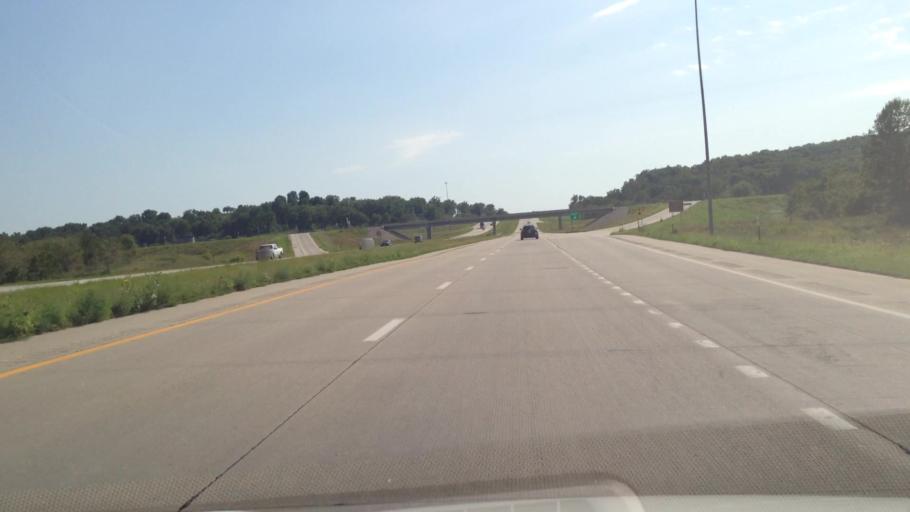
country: US
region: Kansas
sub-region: Linn County
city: Pleasanton
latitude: 38.2659
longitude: -94.6704
